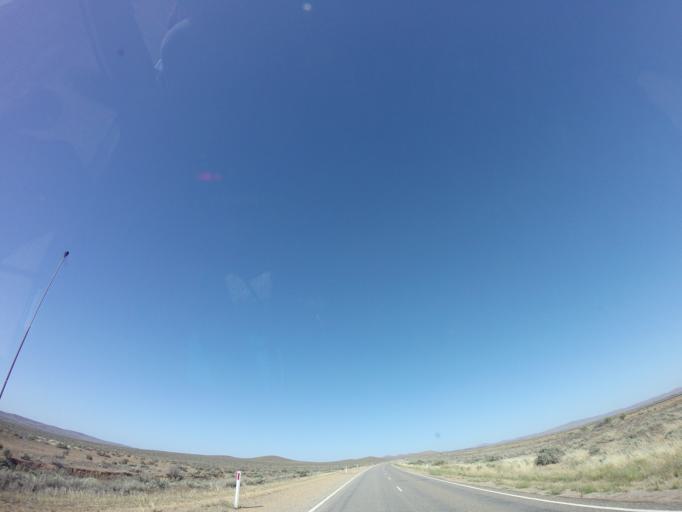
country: AU
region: South Australia
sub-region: Peterborough
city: Peterborough
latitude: -32.5415
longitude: 139.6635
